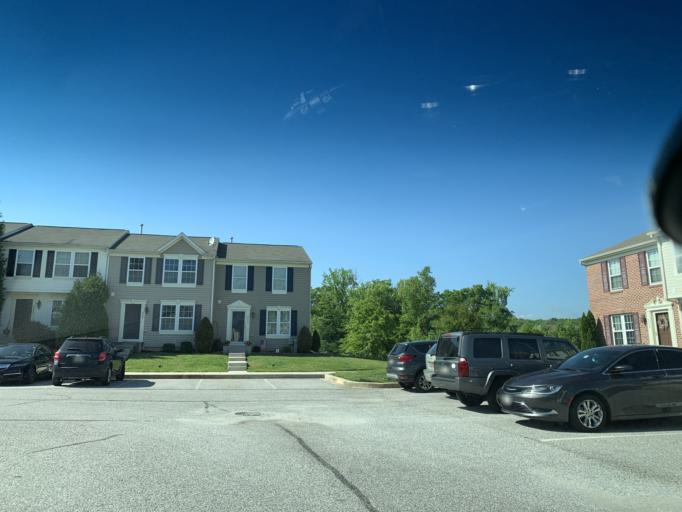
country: US
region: Maryland
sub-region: Harford County
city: Perryman
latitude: 39.4945
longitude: -76.2195
